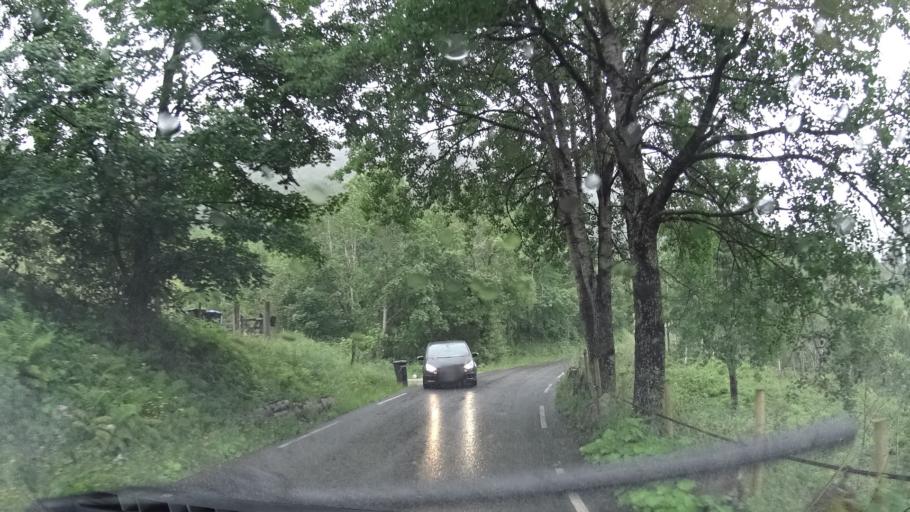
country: NO
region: Sogn og Fjordane
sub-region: Vik
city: Vik
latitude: 60.8313
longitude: 6.6785
